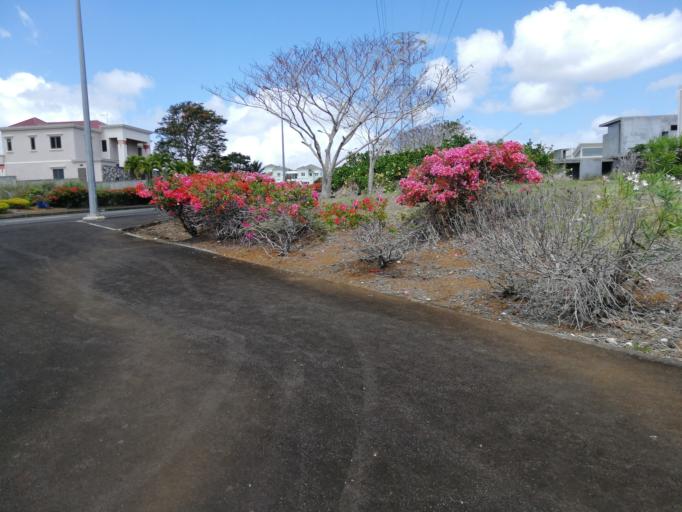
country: MU
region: Plaines Wilhems
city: Ebene
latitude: -20.2308
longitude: 57.4806
